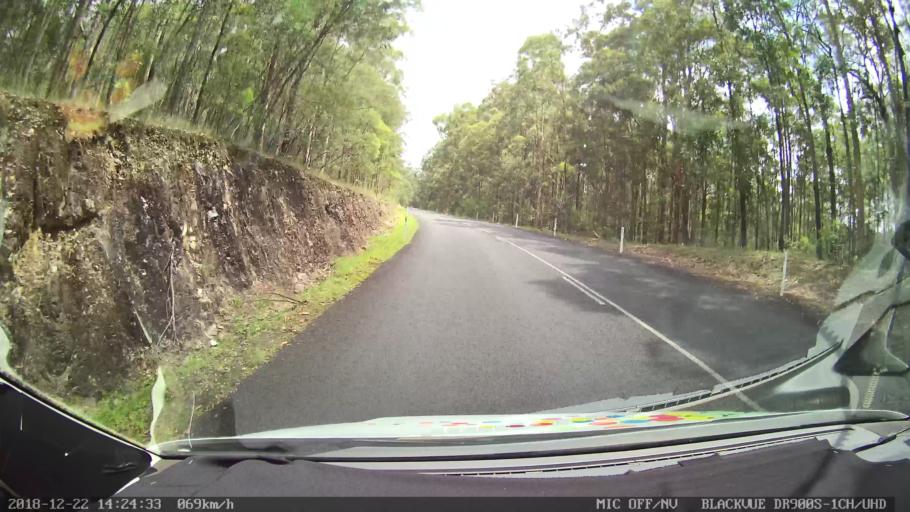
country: AU
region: New South Wales
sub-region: Bellingen
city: Dorrigo
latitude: -30.0443
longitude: 152.6430
